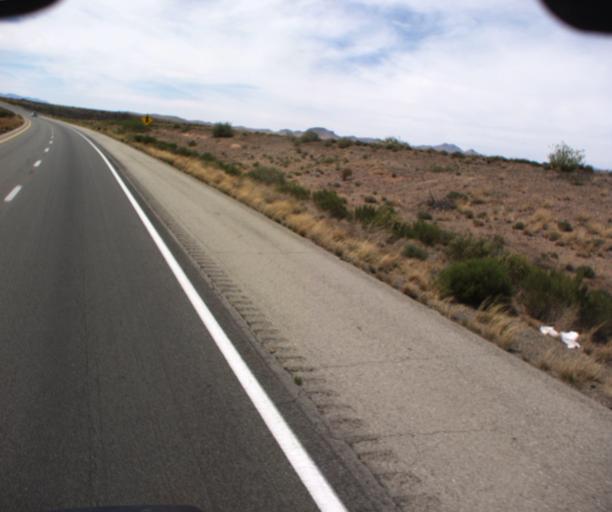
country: US
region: Arizona
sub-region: Cochise County
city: Willcox
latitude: 32.3627
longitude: -109.6227
